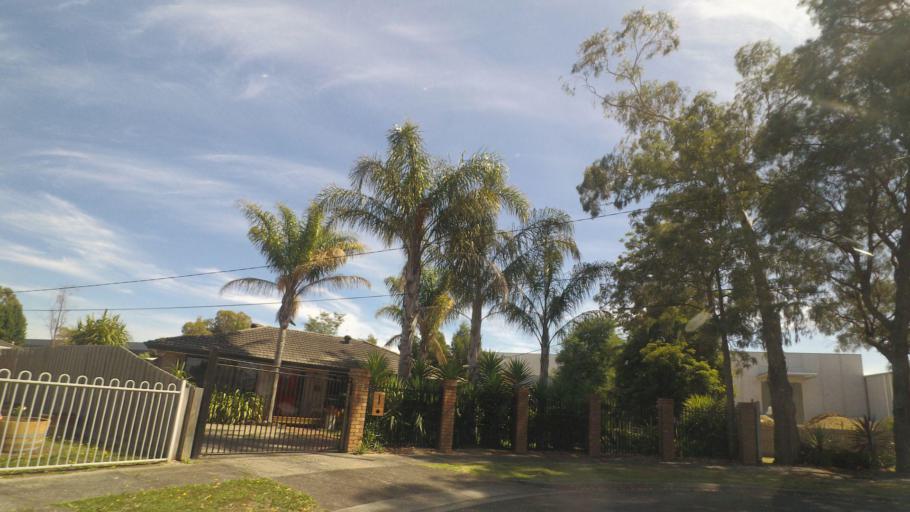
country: AU
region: Victoria
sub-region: Maroondah
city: Croydon North
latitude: -37.7717
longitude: 145.3020
